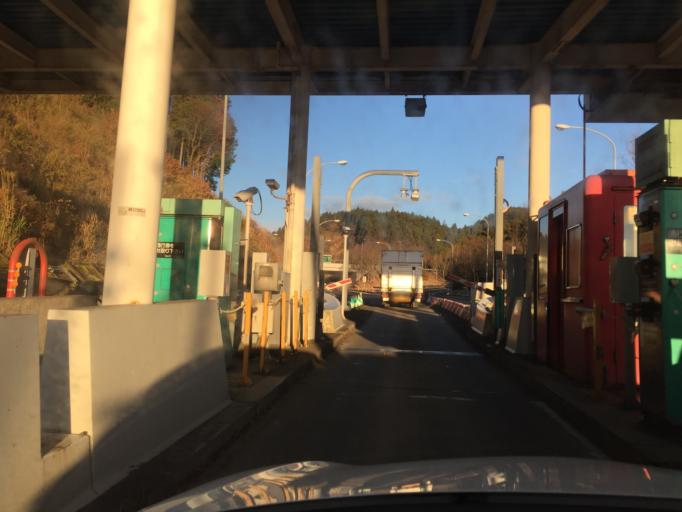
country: JP
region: Ibaraki
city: Kitaibaraki
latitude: 36.7967
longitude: 140.7266
